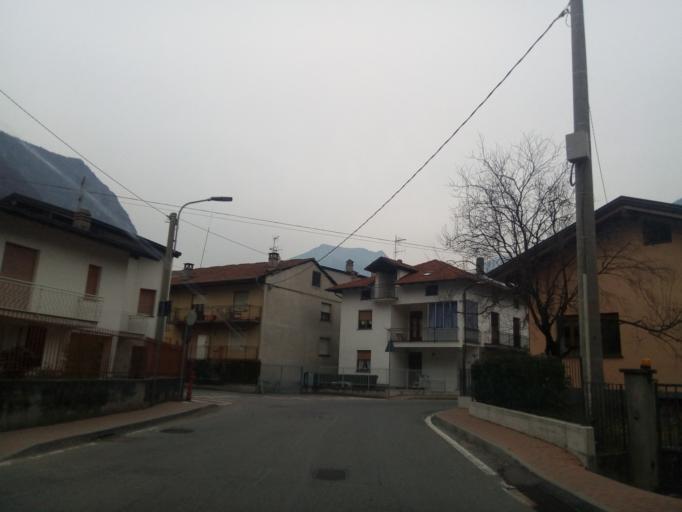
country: IT
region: Piedmont
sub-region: Provincia di Torino
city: Quincinetto
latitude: 45.5624
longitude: 7.8092
